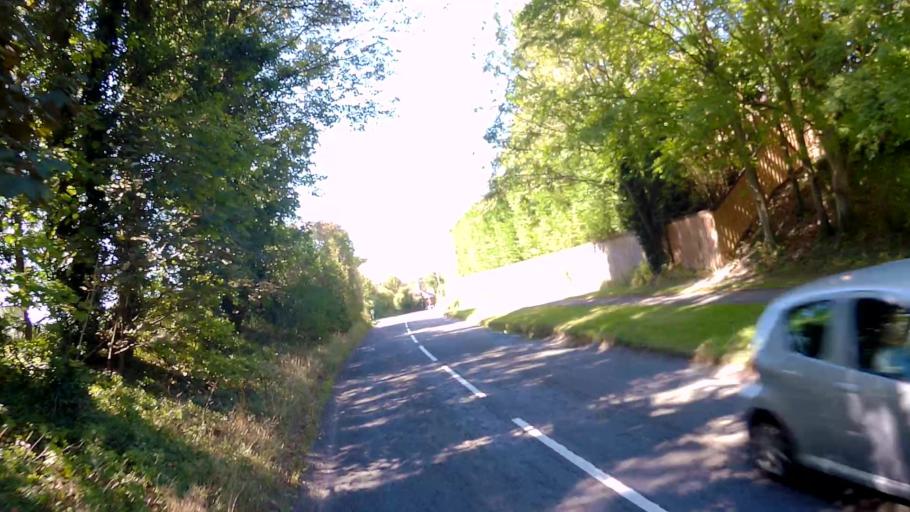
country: GB
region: England
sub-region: Hampshire
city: Overton
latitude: 51.2311
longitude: -1.3256
